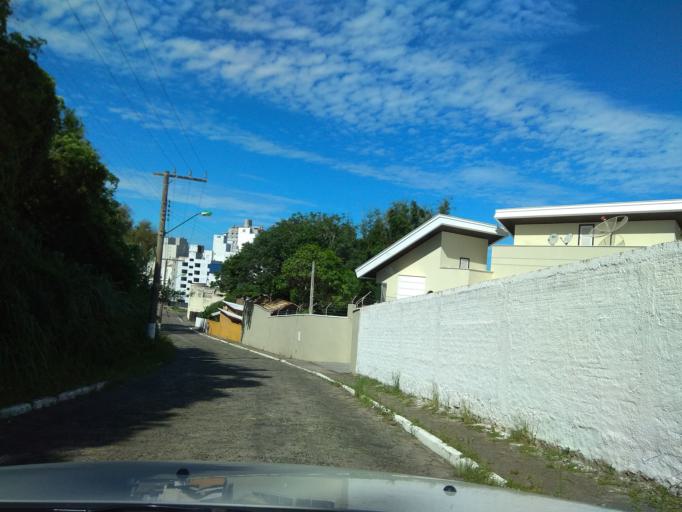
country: BR
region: Santa Catarina
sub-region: Laguna
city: Laguna
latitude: -28.4801
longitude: -48.7726
